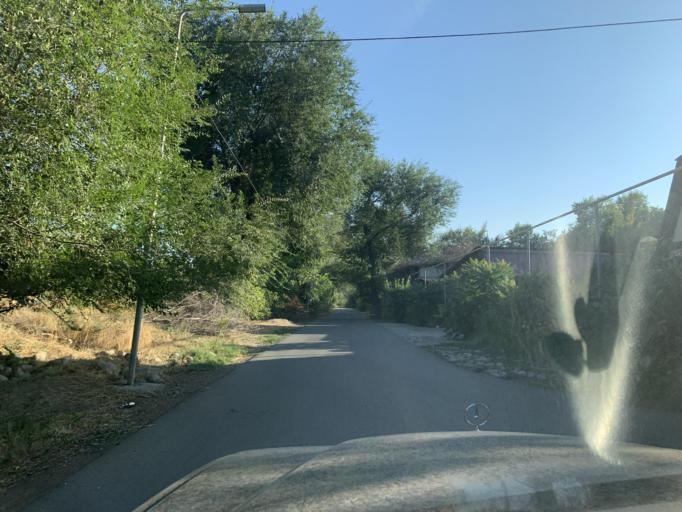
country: KZ
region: Almaty Oblysy
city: Energeticheskiy
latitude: 43.3909
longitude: 76.9997
